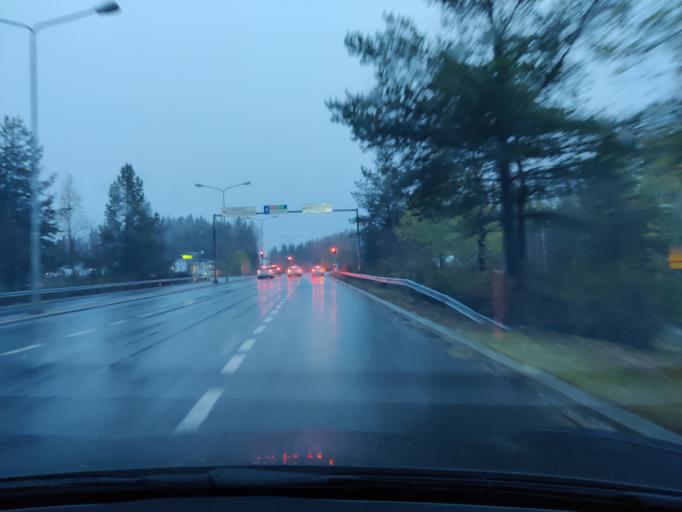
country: FI
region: Northern Savo
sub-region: Kuopio
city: Kuopio
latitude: 62.8372
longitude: 27.6566
